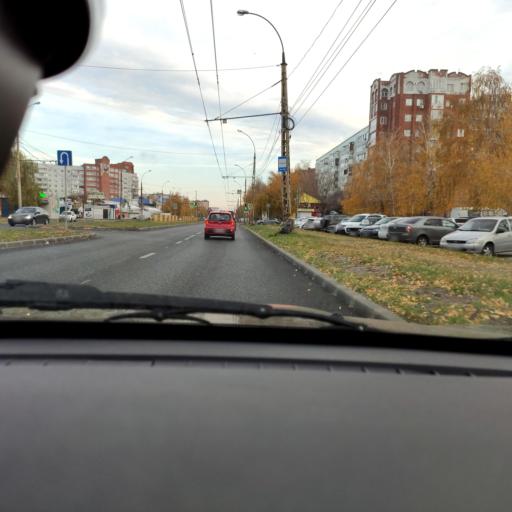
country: RU
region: Samara
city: Tol'yatti
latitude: 53.5286
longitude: 49.3275
